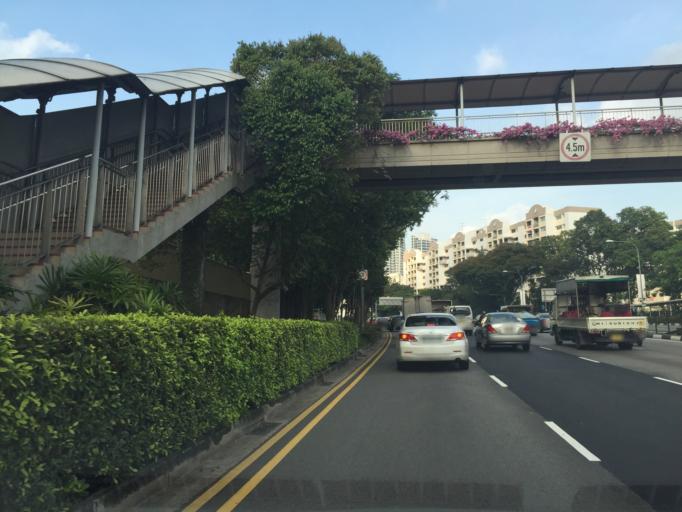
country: SG
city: Singapore
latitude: 1.3192
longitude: 103.8102
